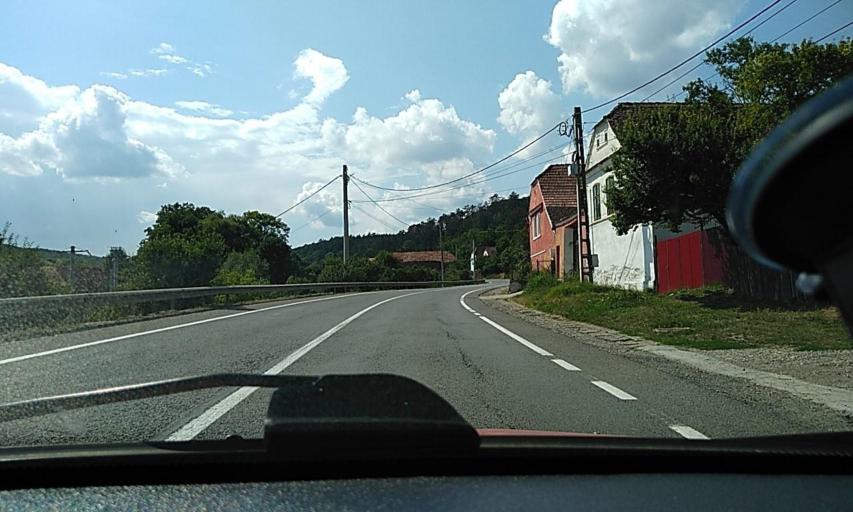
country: RO
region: Brasov
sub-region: Oras Rupea
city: Fiser
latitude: 46.0786
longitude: 25.1424
